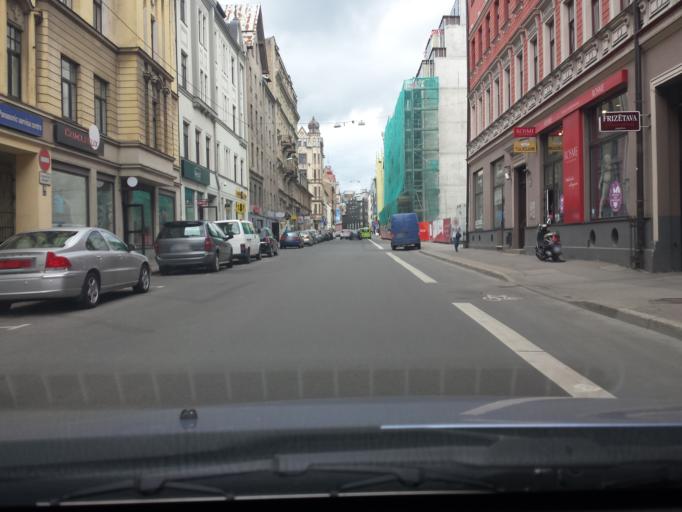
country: LV
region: Riga
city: Riga
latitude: 56.9525
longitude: 24.1222
